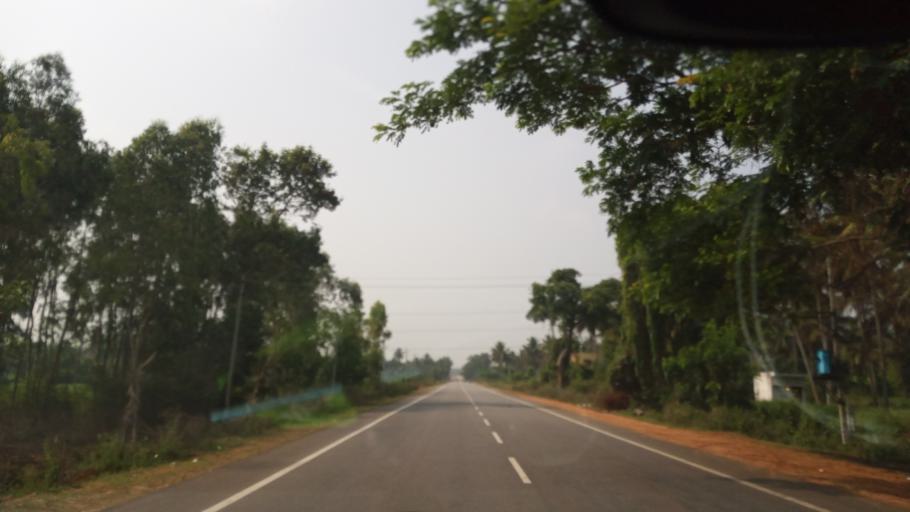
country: IN
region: Karnataka
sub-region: Mandya
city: Pandavapura
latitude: 12.5353
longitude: 76.6706
